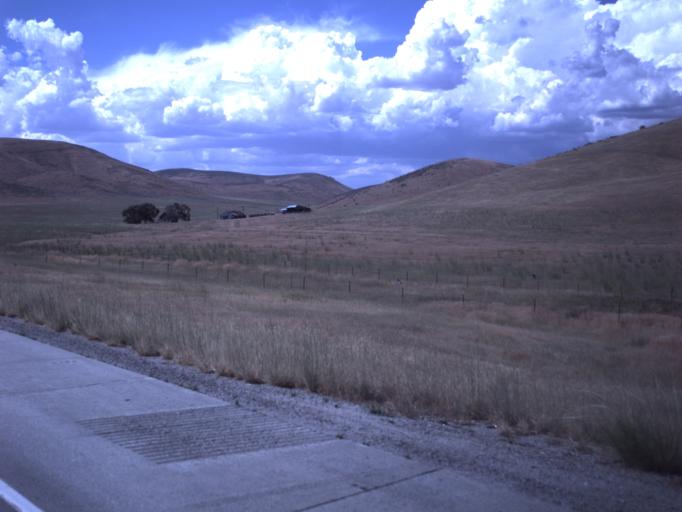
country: US
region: Utah
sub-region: Box Elder County
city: Garland
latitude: 41.8078
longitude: -112.3349
